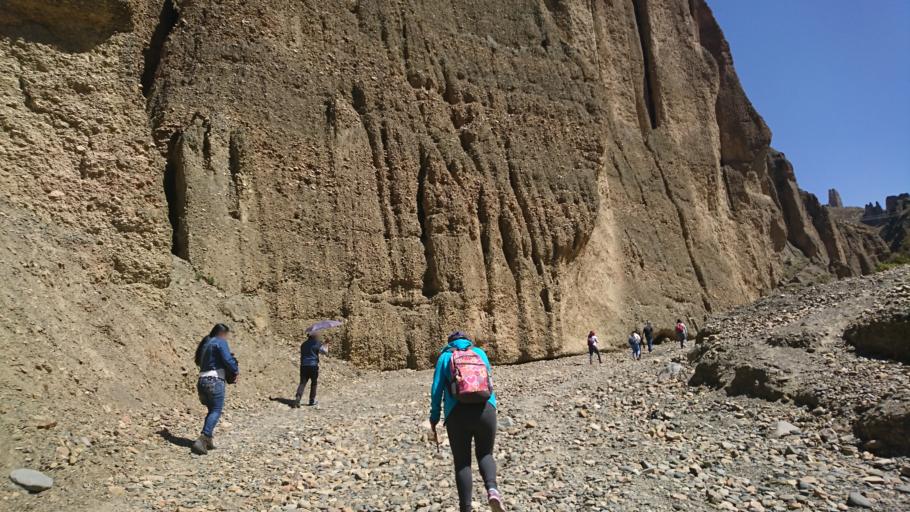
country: BO
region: La Paz
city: La Paz
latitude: -16.5409
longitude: -68.0053
